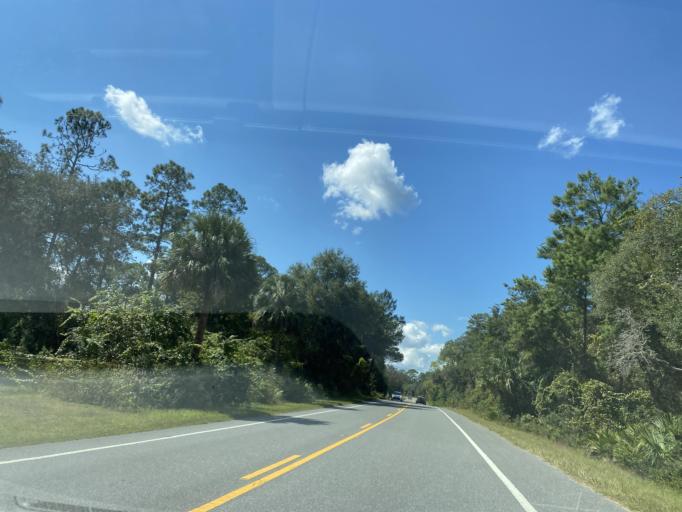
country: US
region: Florida
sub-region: Lake County
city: Lake Mack-Forest Hills
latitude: 29.0174
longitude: -81.4808
